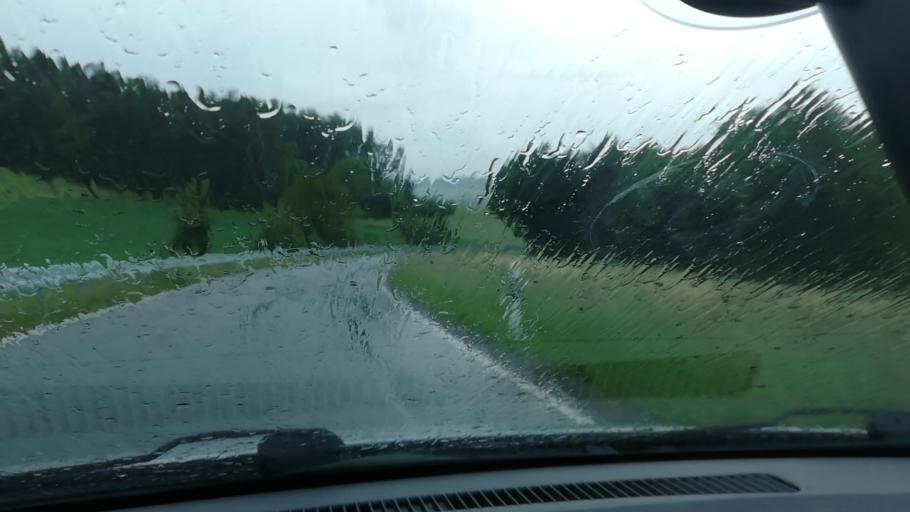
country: DE
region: Bavaria
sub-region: Regierungsbezirk Unterfranken
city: Thungen
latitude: 50.0080
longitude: 9.8845
